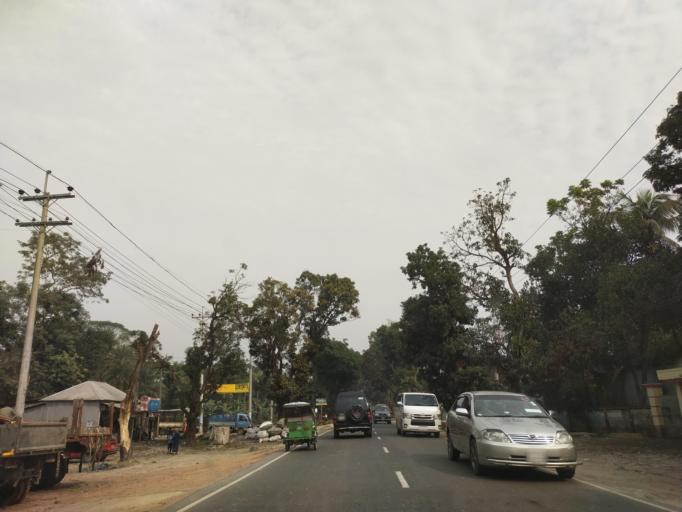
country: BD
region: Dhaka
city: Narsingdi
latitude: 23.9829
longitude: 90.7344
